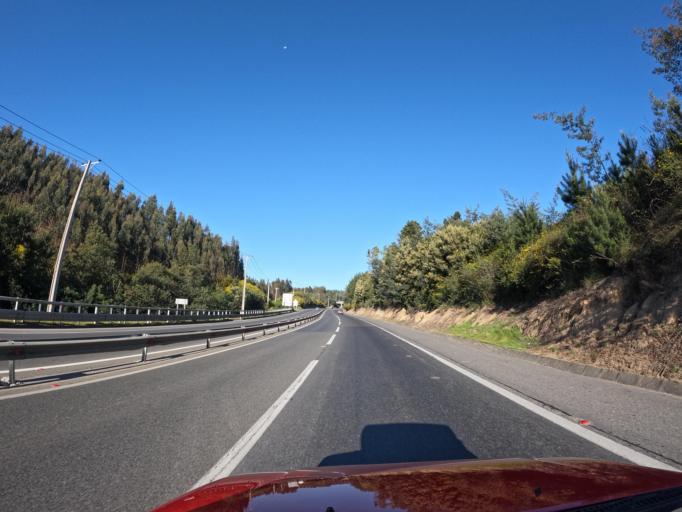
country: CL
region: Biobio
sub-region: Provincia de Concepcion
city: Penco
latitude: -36.7526
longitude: -72.9845
